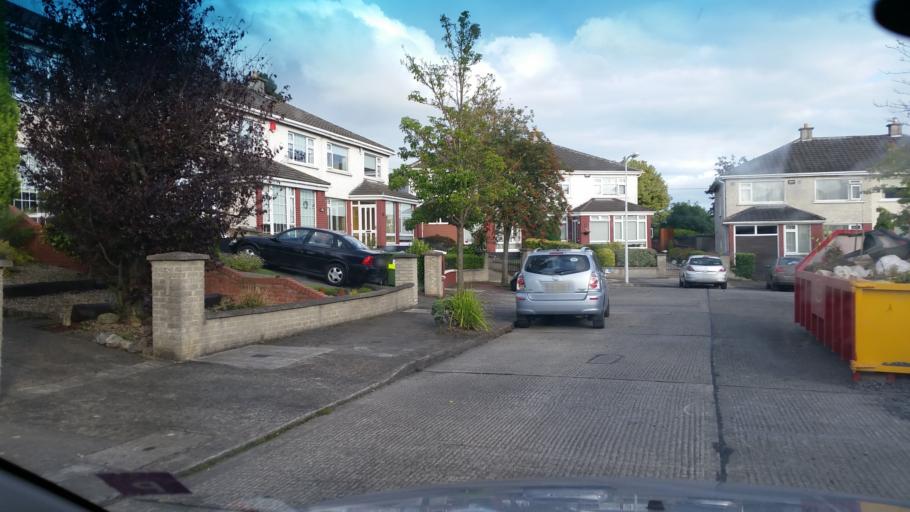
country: IE
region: Leinster
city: Drumcondra
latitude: 53.3796
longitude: -6.2510
